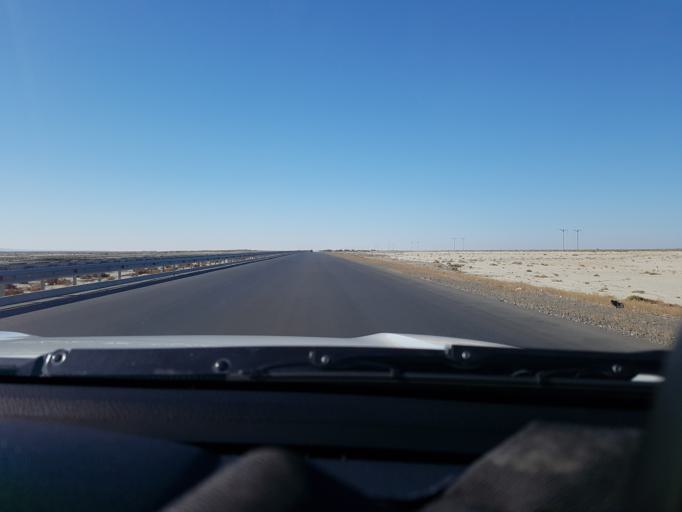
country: TM
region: Balkan
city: Gazanjyk
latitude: 39.2500
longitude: 55.0985
